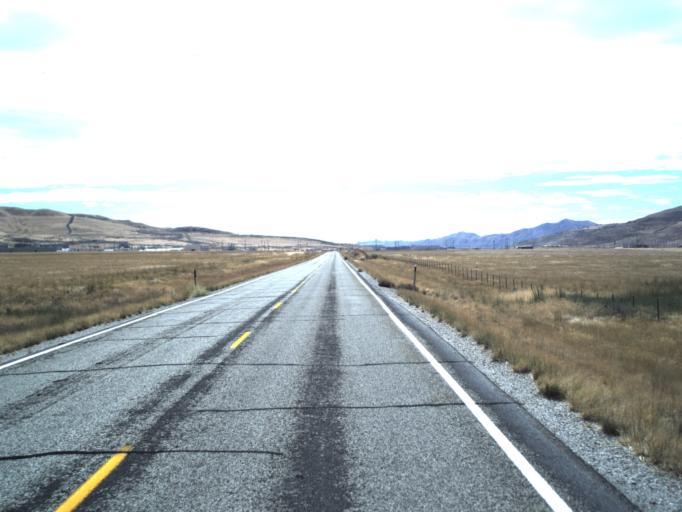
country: US
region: Utah
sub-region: Box Elder County
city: Tremonton
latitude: 41.7310
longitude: -112.4339
